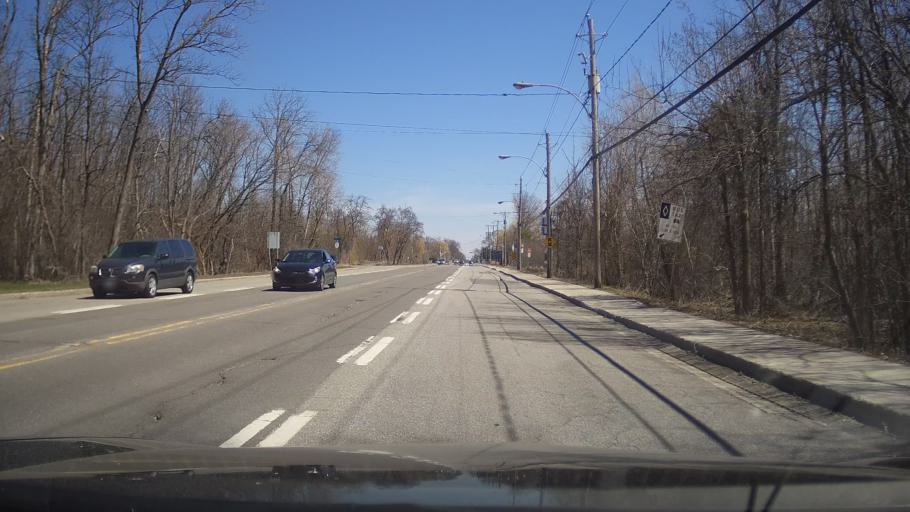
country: CA
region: Ontario
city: Bells Corners
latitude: 45.4023
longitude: -75.8068
